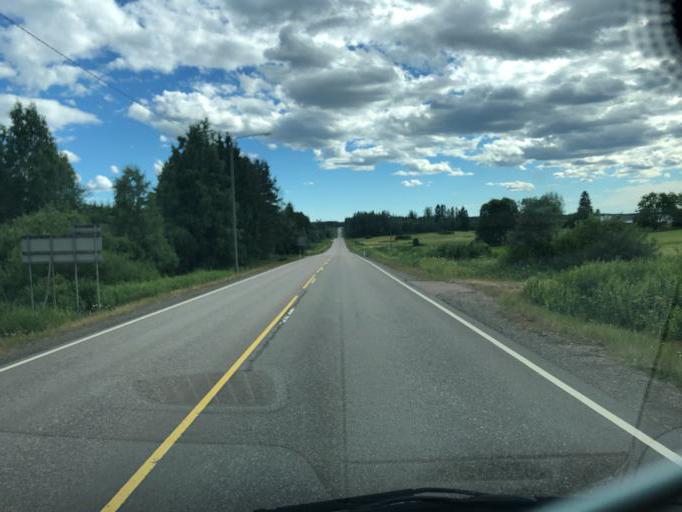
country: FI
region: Southern Savonia
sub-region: Mikkeli
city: Maentyharju
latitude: 61.0874
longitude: 27.0658
